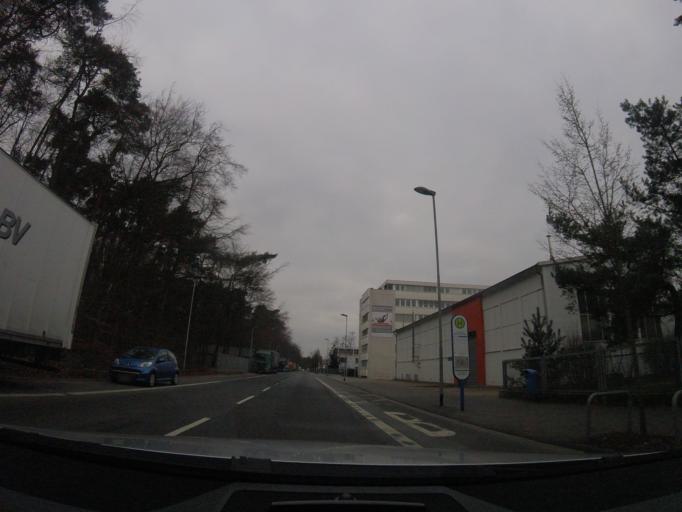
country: DE
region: Hesse
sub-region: Regierungsbezirk Darmstadt
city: Neu Isenburg
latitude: 50.0437
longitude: 8.6777
